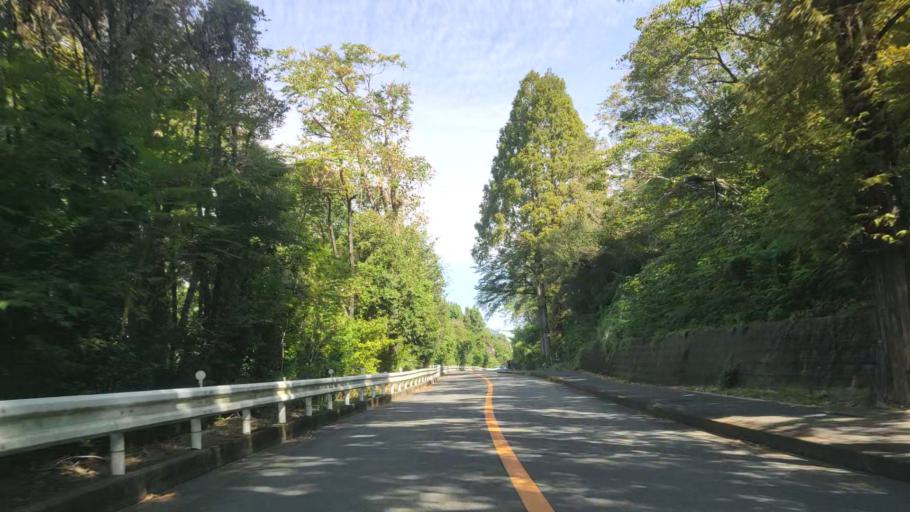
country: JP
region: Osaka
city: Ibaraki
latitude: 34.8171
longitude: 135.5193
